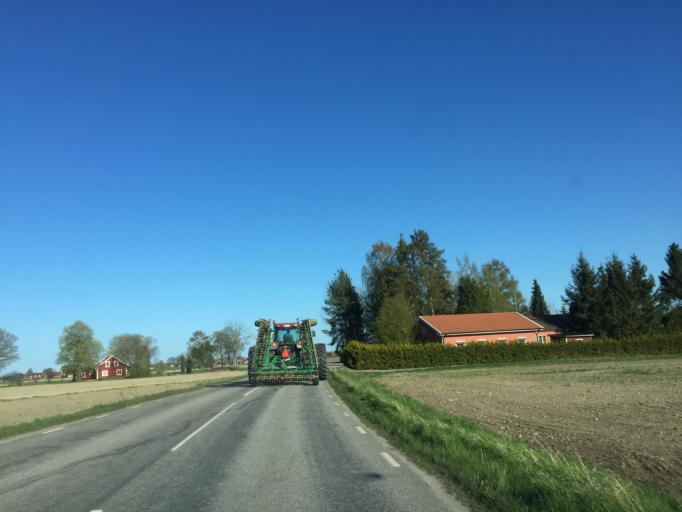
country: SE
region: OErebro
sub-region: Orebro Kommun
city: Odensbacken
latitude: 59.2045
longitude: 15.5278
